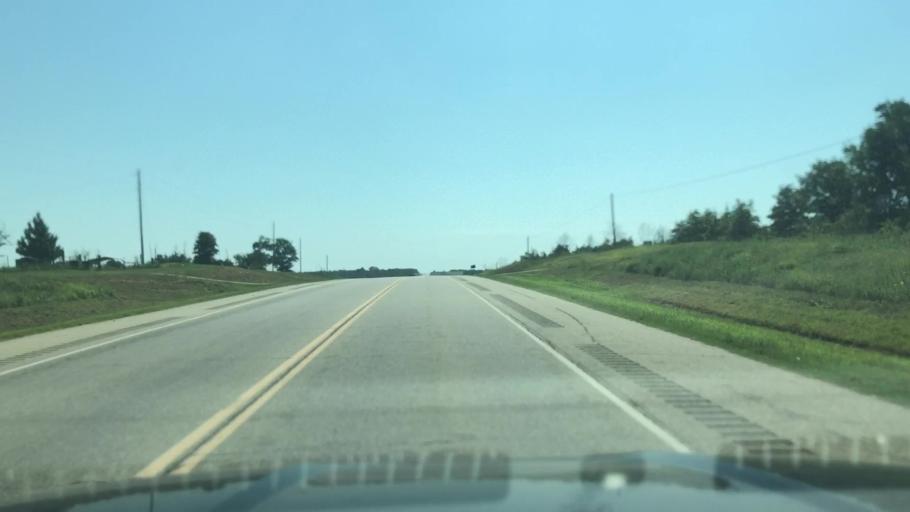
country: US
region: Oklahoma
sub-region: Creek County
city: Mannford
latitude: 36.0031
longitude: -96.4349
